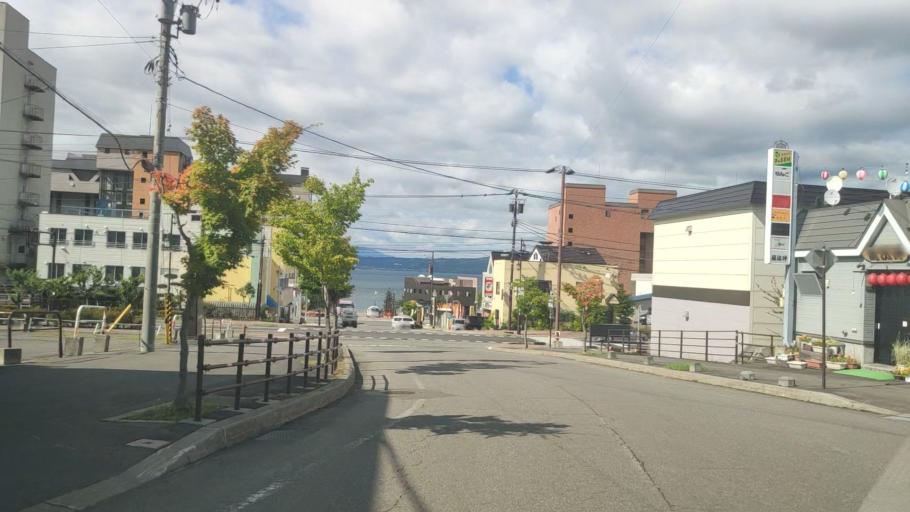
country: JP
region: Hokkaido
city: Date
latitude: 42.5642
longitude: 140.8230
